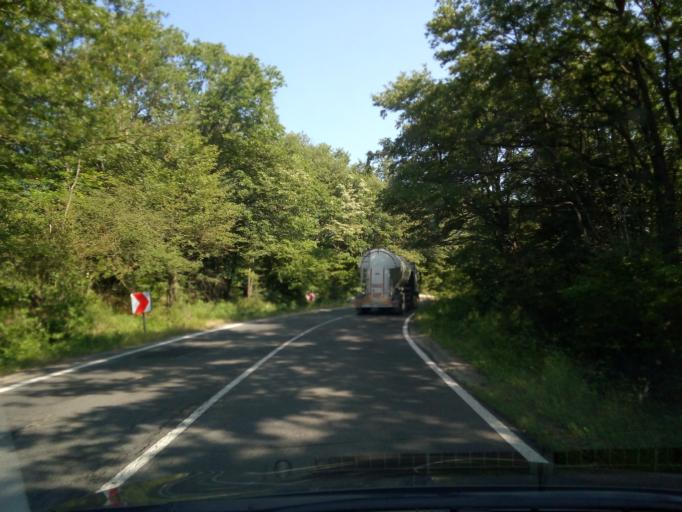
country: BG
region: Burgas
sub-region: Obshtina Nesebur
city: Sveti Vlas
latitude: 42.7732
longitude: 27.7676
